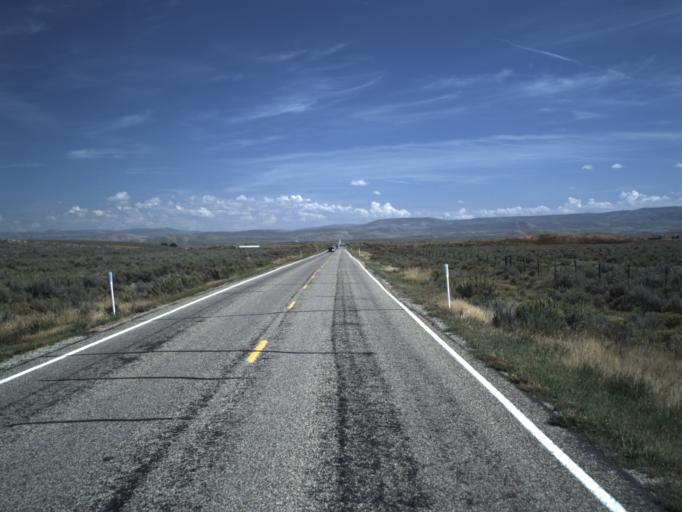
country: US
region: Utah
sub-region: Rich County
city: Randolph
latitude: 41.7710
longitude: -111.1388
